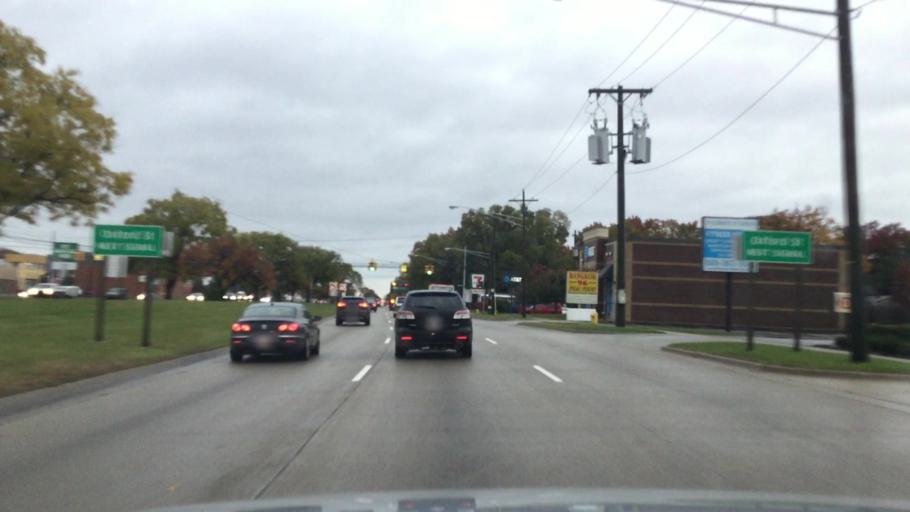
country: US
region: Michigan
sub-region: Wayne County
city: Inkster
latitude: 42.2945
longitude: -83.2716
